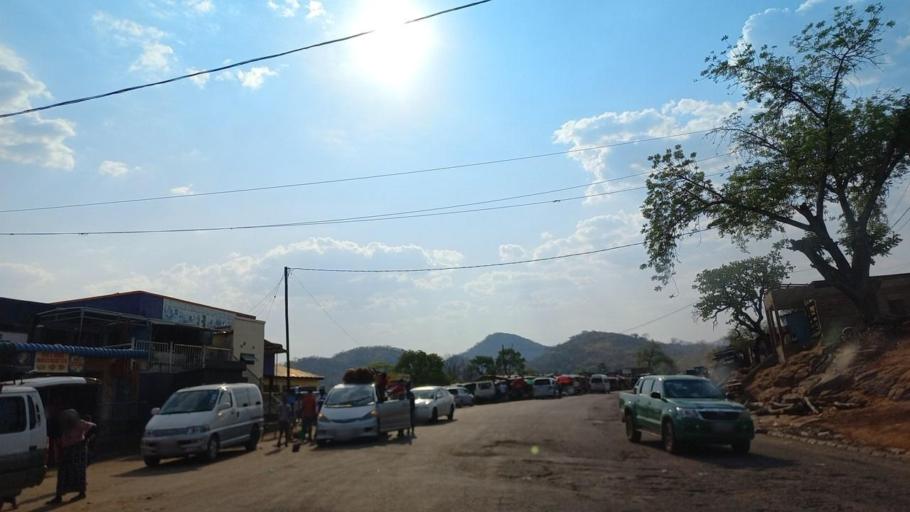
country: ZM
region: Lusaka
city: Luangwa
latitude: -14.9853
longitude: 30.2052
